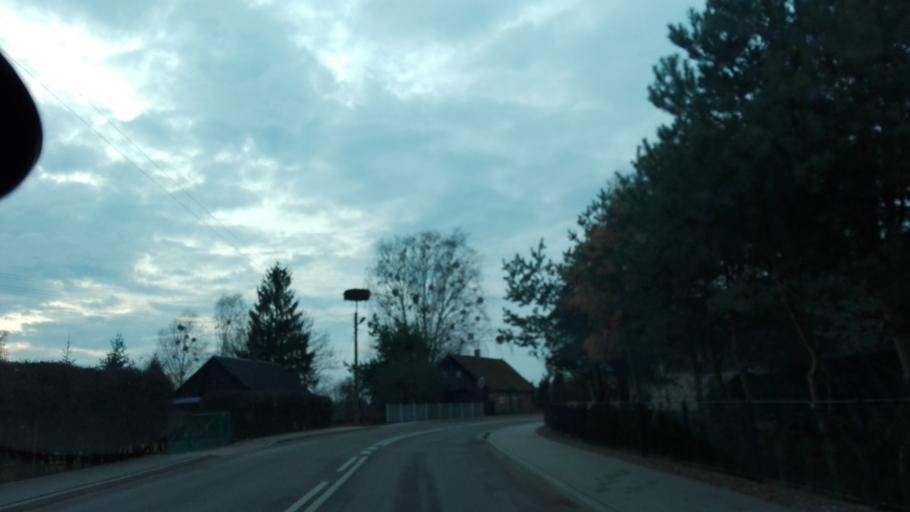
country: PL
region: Lublin Voivodeship
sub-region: Powiat bialski
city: Slawatycze
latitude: 51.7172
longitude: 23.5004
